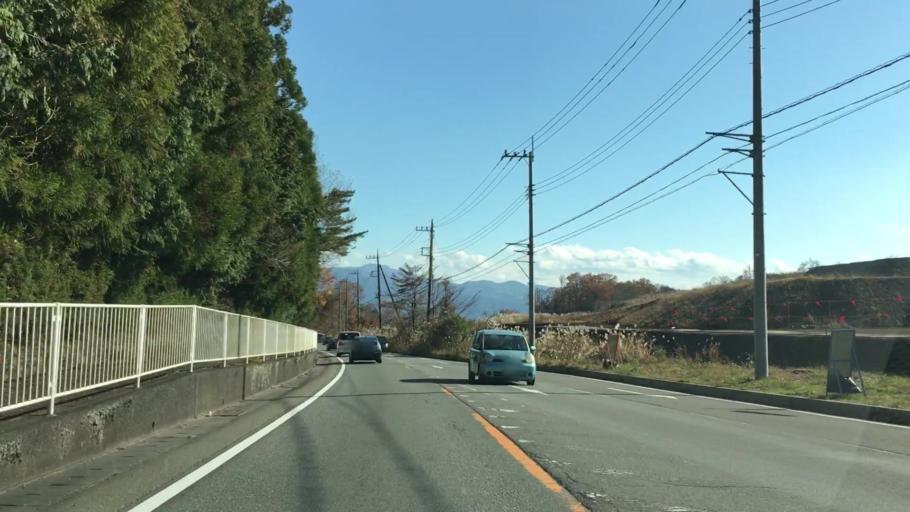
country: JP
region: Shizuoka
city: Gotemba
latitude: 35.3466
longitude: 138.8799
